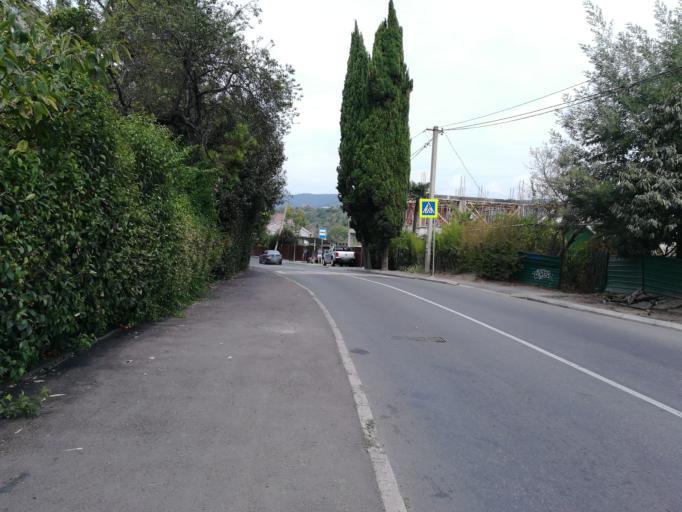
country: RU
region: Krasnodarskiy
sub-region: Sochi City
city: Sochi
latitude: 43.5915
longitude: 39.7407
